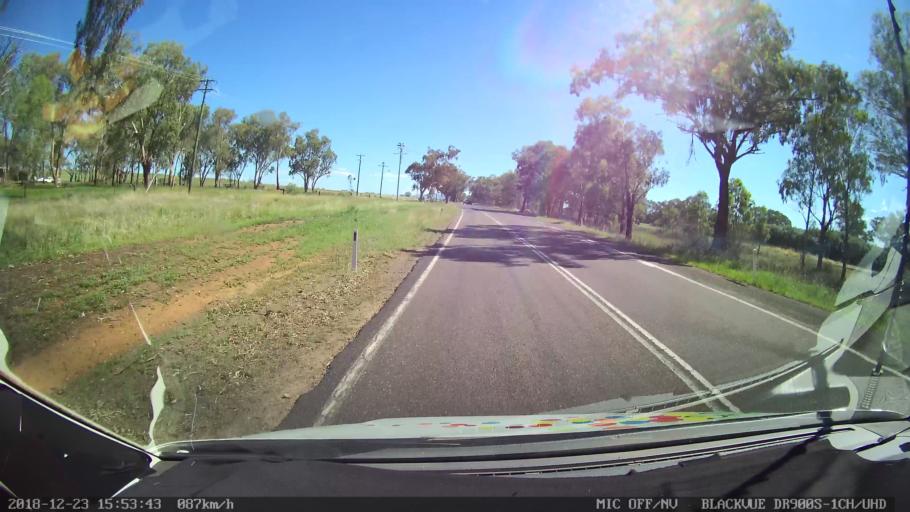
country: AU
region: New South Wales
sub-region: Tamworth Municipality
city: Phillip
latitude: -31.1367
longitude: 150.8795
